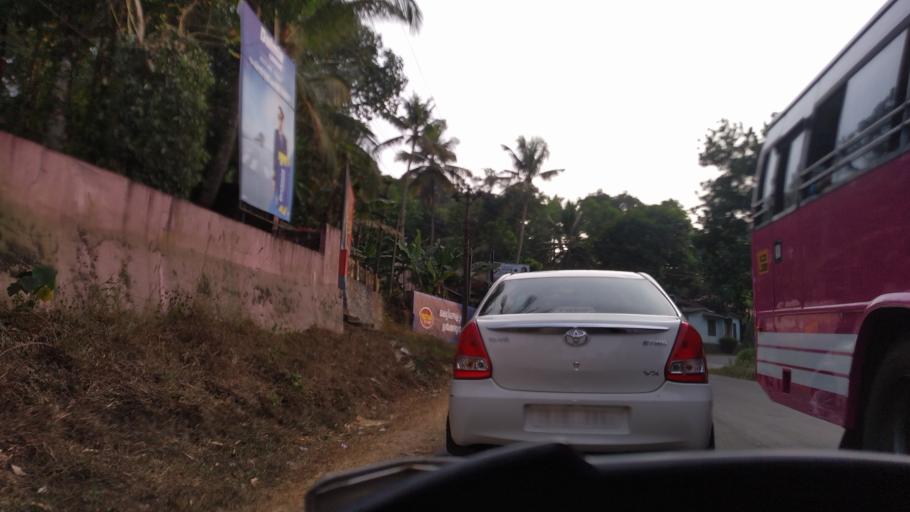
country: IN
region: Kerala
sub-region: Kottayam
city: Erattupetta
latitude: 9.5683
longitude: 76.7162
